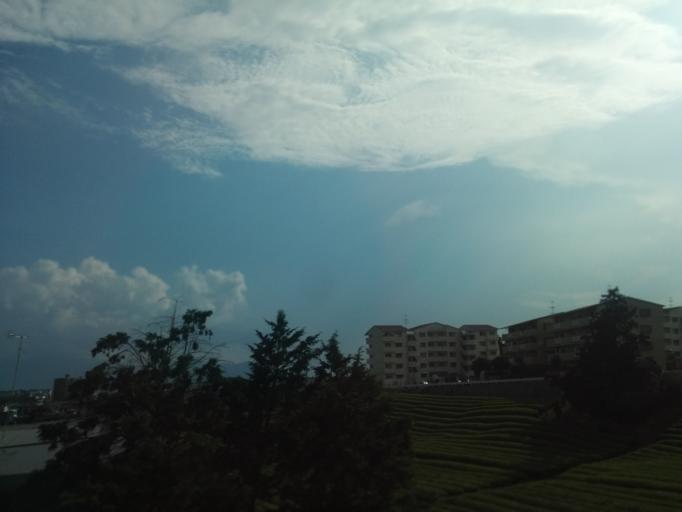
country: JP
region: Shizuoka
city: Numazu
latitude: 35.1273
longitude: 138.8338
